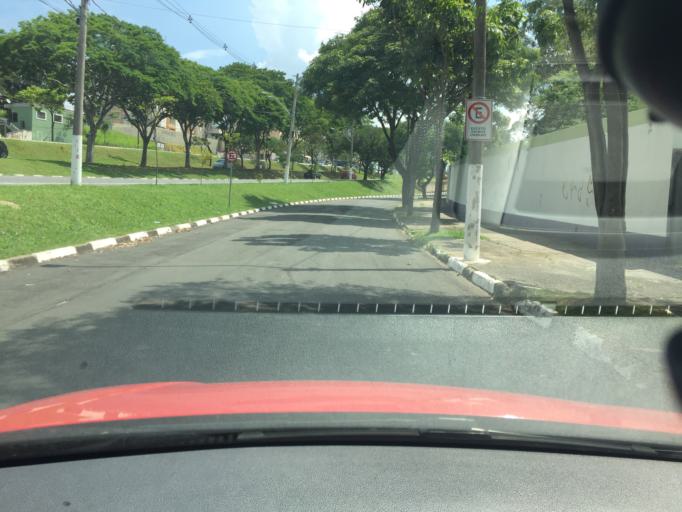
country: BR
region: Sao Paulo
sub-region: Valinhos
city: Valinhos
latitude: -22.9817
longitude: -47.0014
